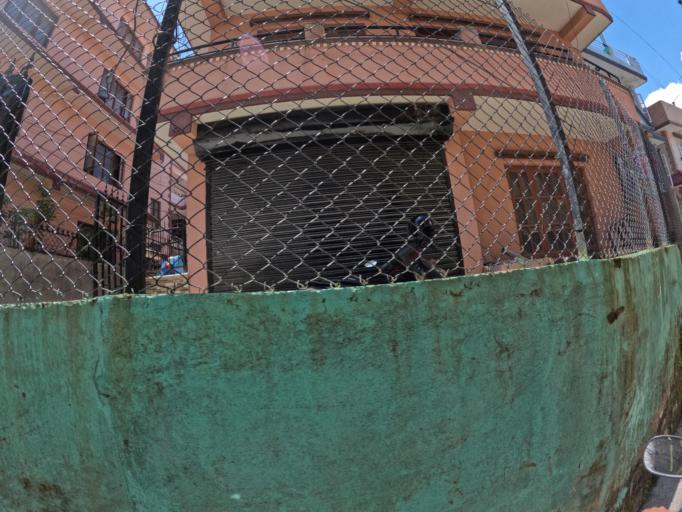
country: NP
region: Central Region
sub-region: Bagmati Zone
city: Kathmandu
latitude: 27.7483
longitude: 85.3274
